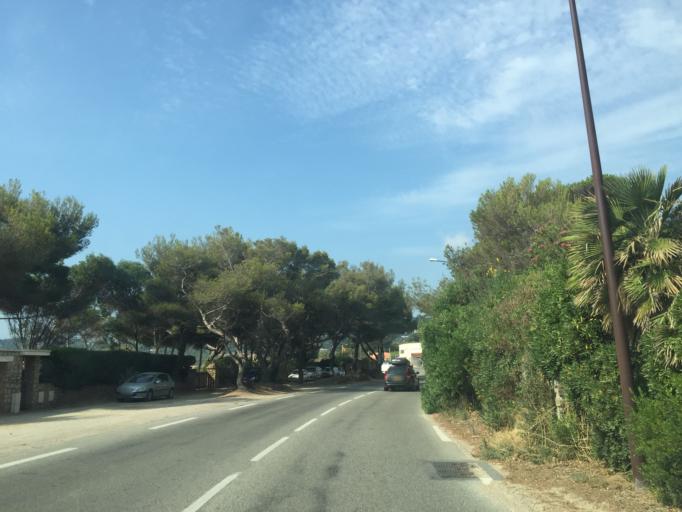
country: FR
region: Provence-Alpes-Cote d'Azur
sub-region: Departement du Var
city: Sainte-Maxime
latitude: 43.3264
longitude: 6.6663
